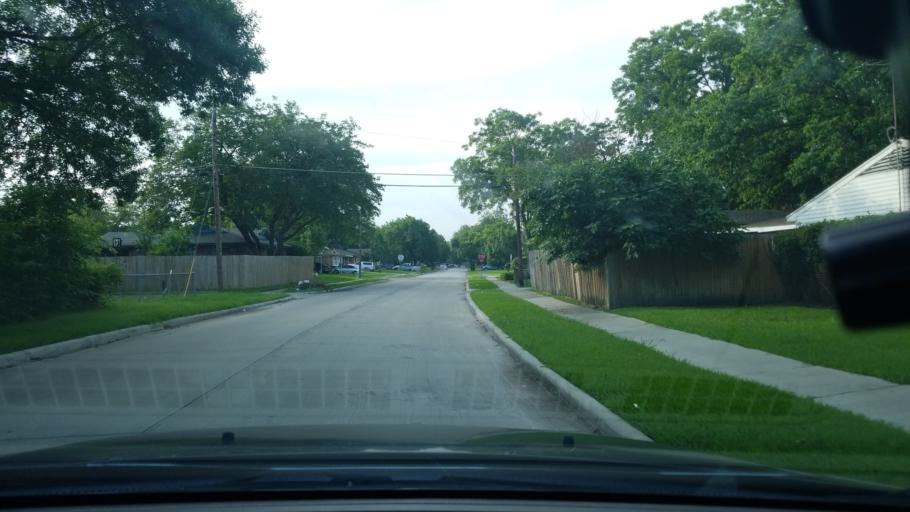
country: US
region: Texas
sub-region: Dallas County
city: Garland
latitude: 32.8313
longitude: -96.6501
